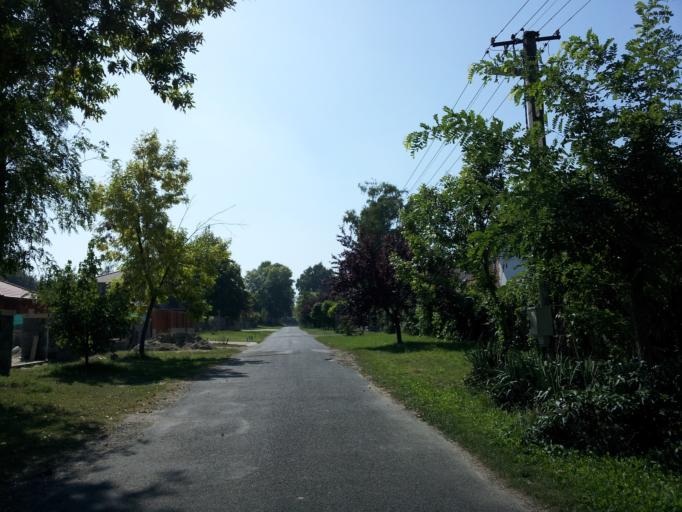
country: HU
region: Somogy
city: Zamardi
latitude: 46.8859
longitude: 17.9581
